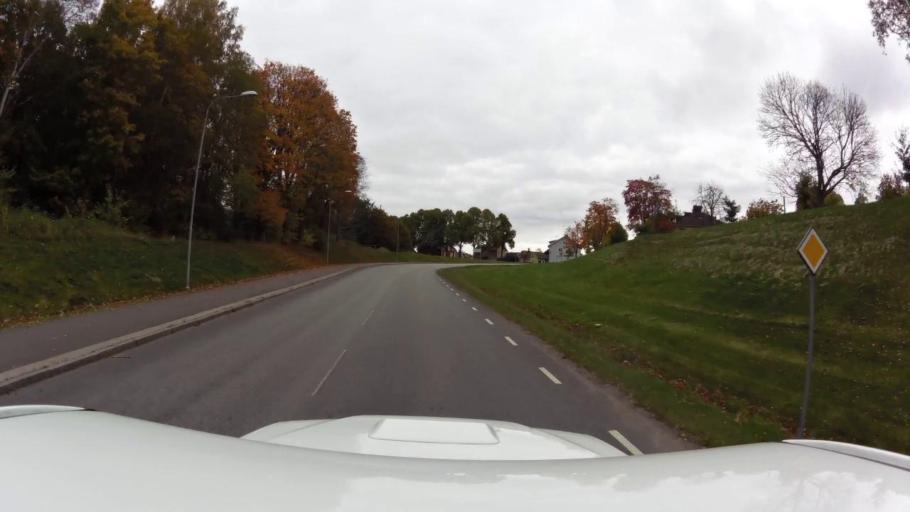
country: SE
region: OEstergoetland
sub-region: Linkopings Kommun
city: Ljungsbro
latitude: 58.5126
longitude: 15.5022
